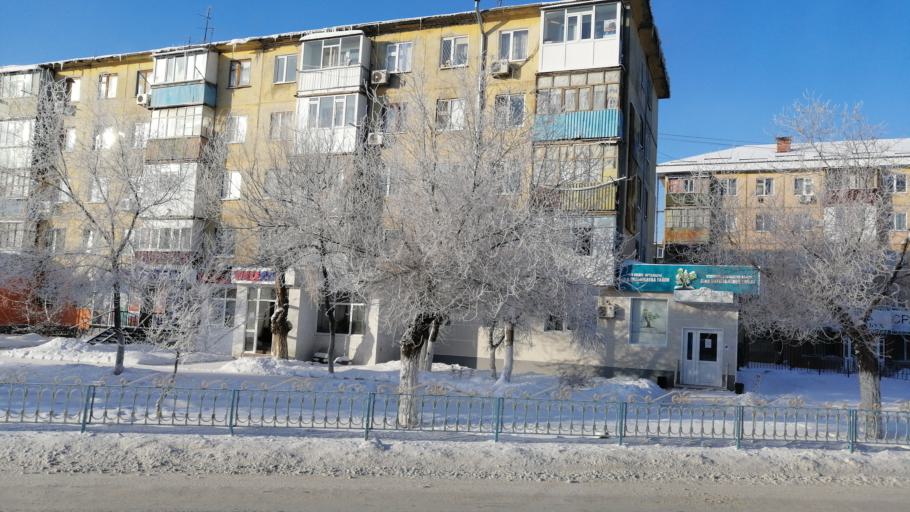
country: KZ
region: Aqtoebe
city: Aqtobe
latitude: 50.3073
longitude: 57.1495
